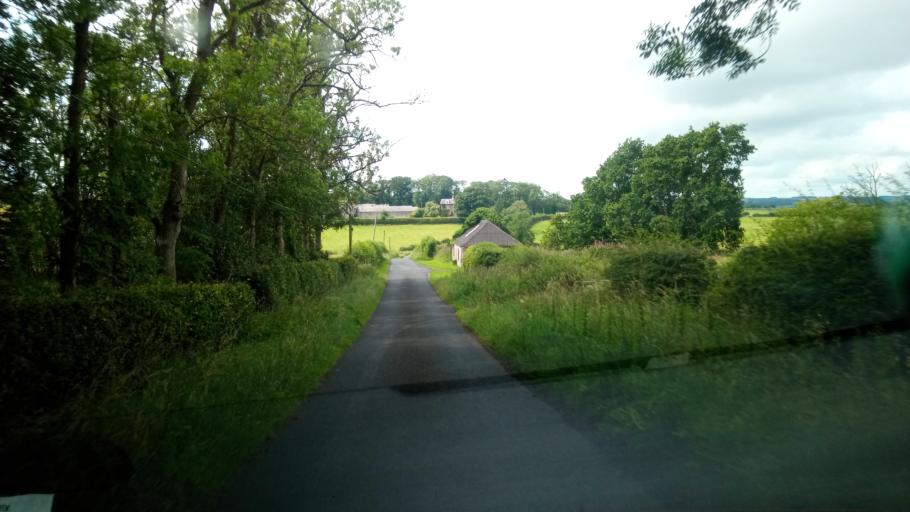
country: GB
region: Scotland
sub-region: The Scottish Borders
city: Hawick
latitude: 55.4397
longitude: -2.6980
